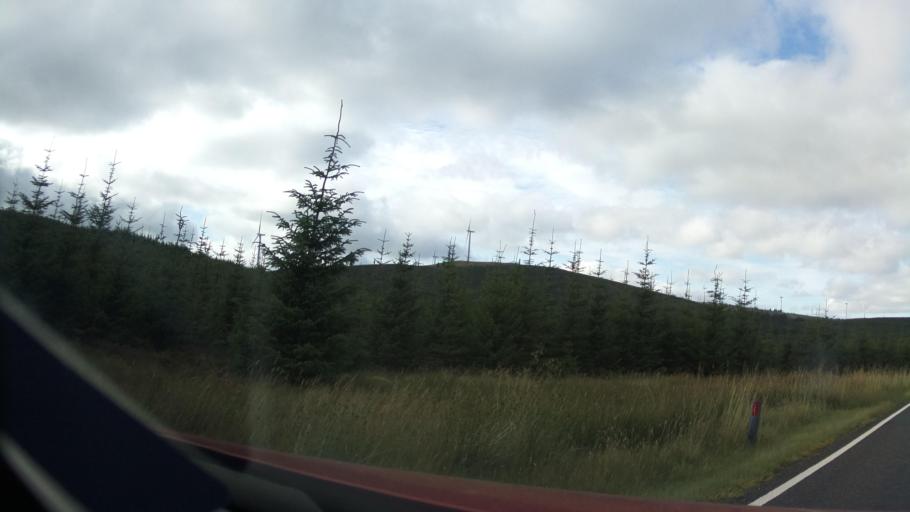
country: GB
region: Scotland
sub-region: Dumfries and Galloway
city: Moffat
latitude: 55.4274
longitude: -3.5046
